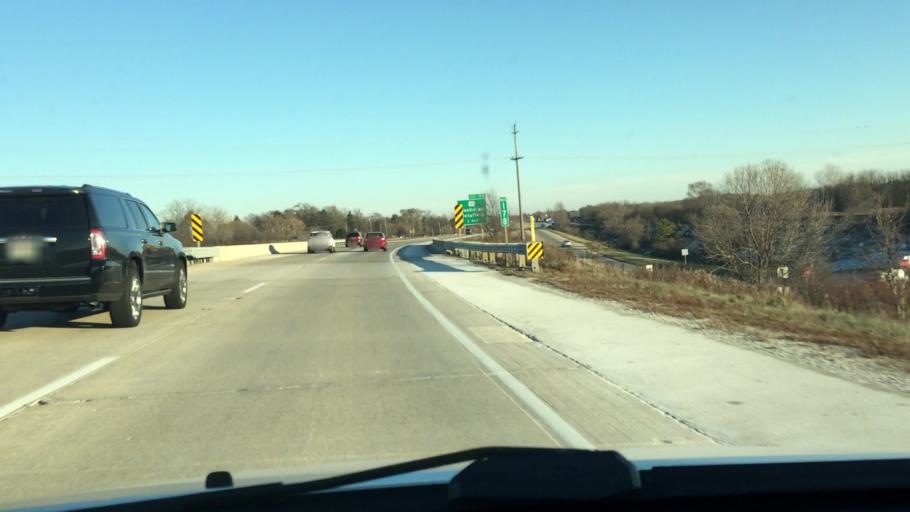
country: US
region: Wisconsin
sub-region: Waukesha County
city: Okauchee Lake
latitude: 43.1077
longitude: -88.4325
